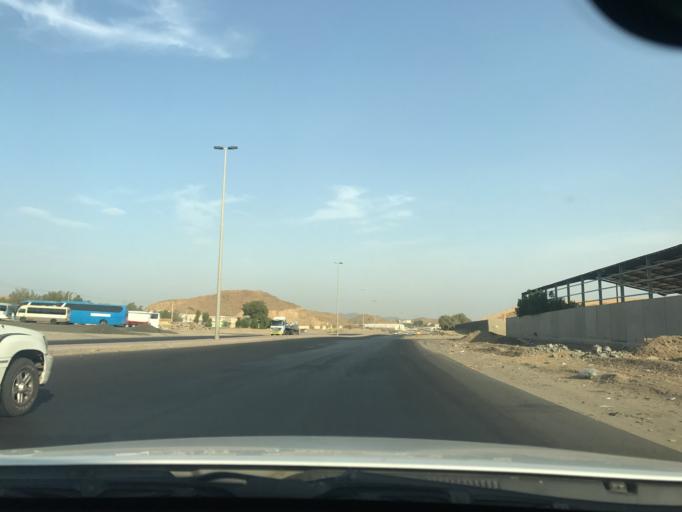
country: SA
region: Makkah
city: Jeddah
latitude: 21.4112
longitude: 39.4226
